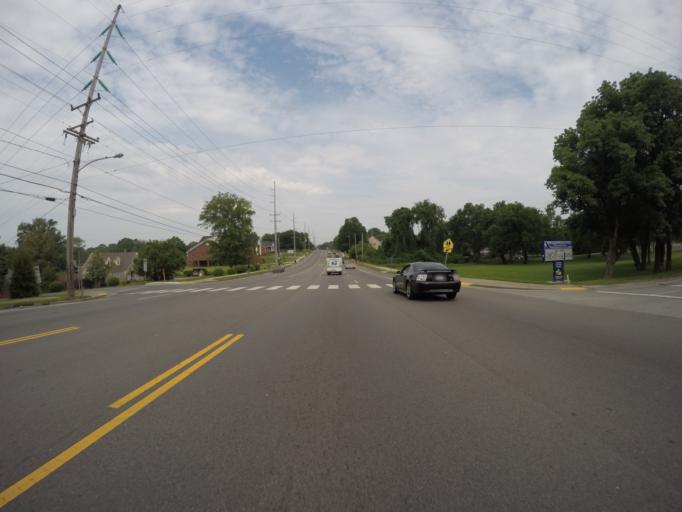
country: US
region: Tennessee
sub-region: Davidson County
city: Goodlettsville
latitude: 36.2637
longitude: -86.7174
